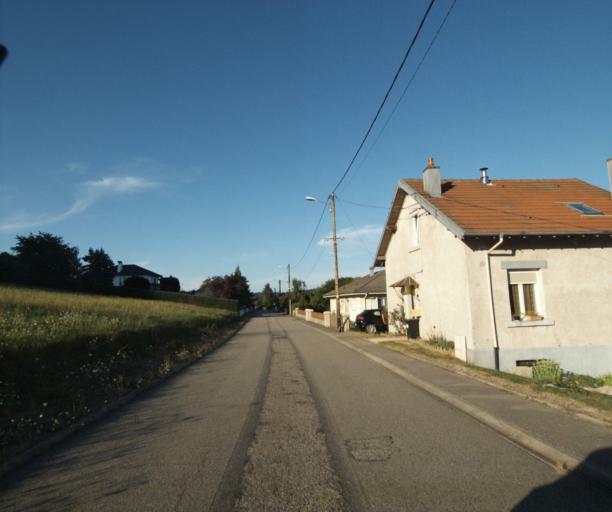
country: FR
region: Lorraine
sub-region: Departement des Vosges
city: Chantraine
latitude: 48.1398
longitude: 6.4482
